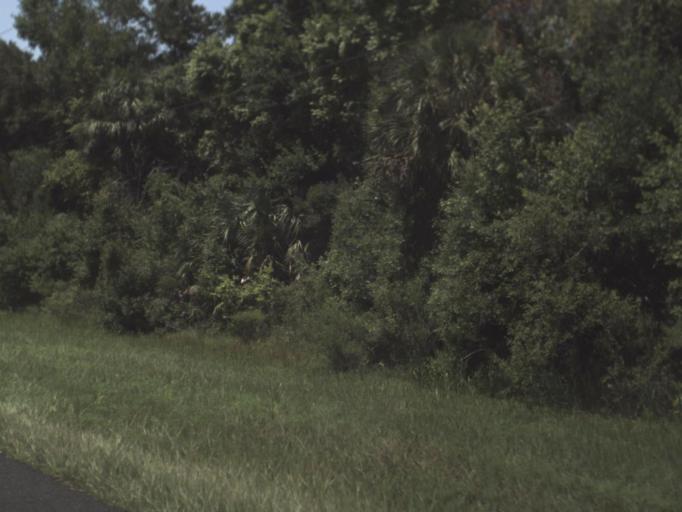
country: US
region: Florida
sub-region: Citrus County
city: Crystal River
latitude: 28.9294
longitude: -82.6154
